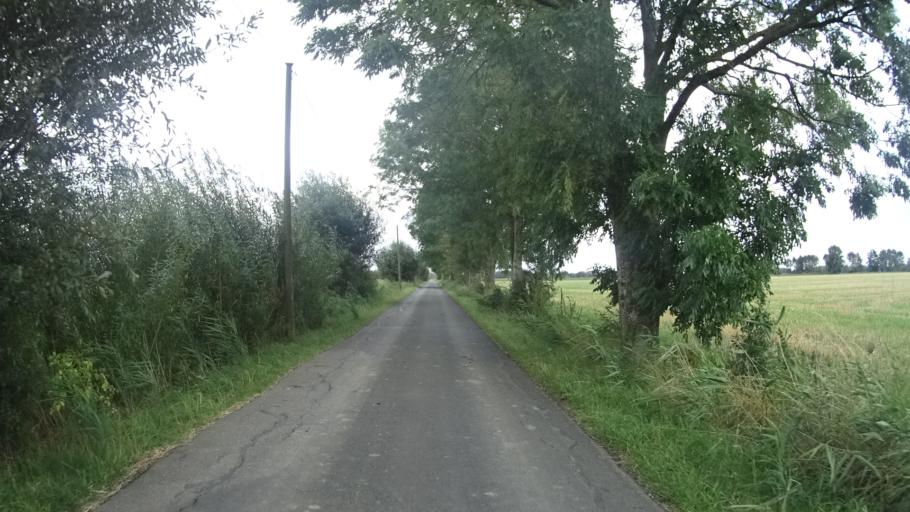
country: DE
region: Schleswig-Holstein
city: Gluckstadt
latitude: 53.7817
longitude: 9.4513
